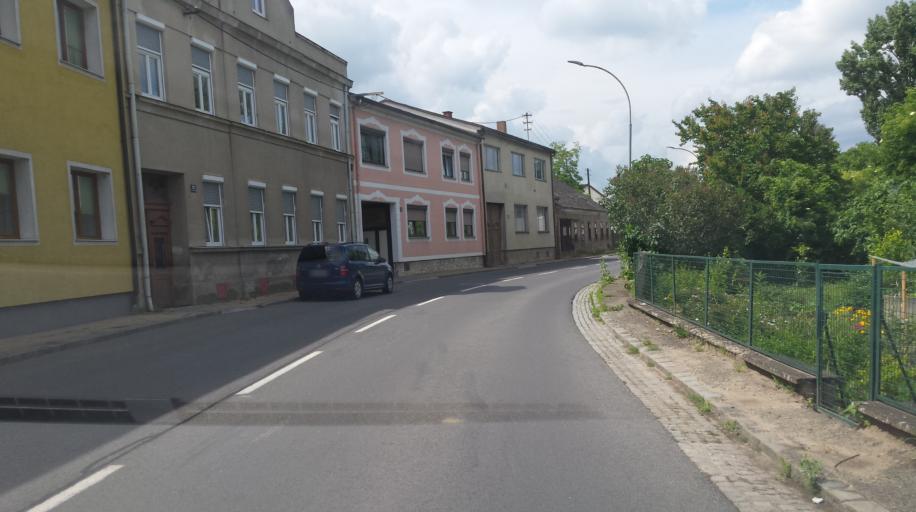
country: AT
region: Lower Austria
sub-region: Politischer Bezirk Ganserndorf
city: Deutsch-Wagram
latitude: 48.2967
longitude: 16.5551
